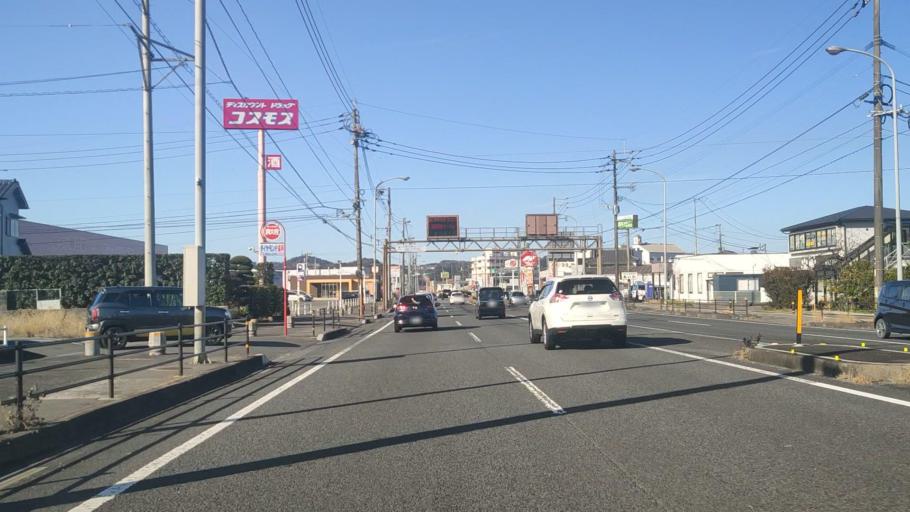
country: JP
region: Oita
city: Oita
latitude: 33.1507
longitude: 131.6570
